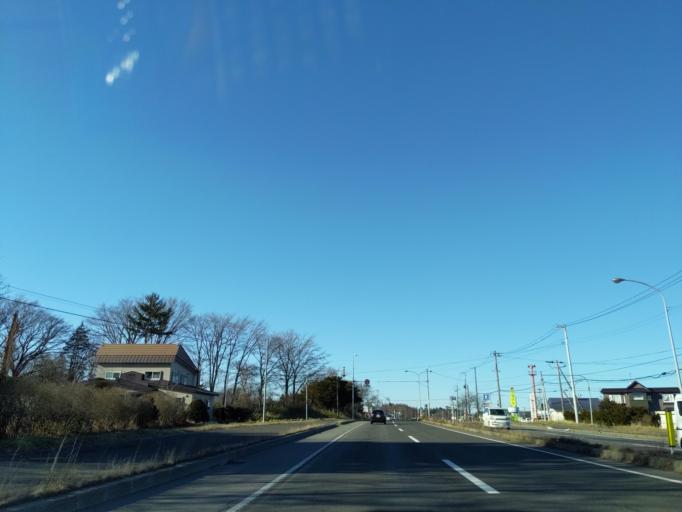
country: JP
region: Hokkaido
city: Kitahiroshima
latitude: 42.9388
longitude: 141.5084
